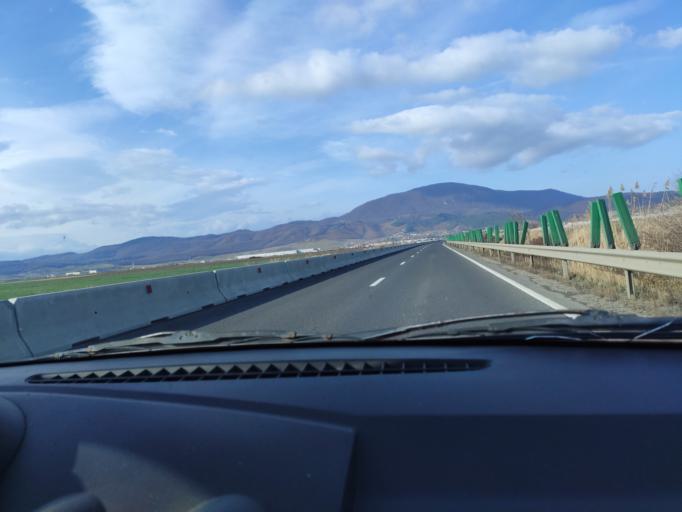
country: RO
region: Brasov
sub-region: Comuna Ghimbav
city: Ghimbav
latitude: 45.6786
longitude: 25.4792
